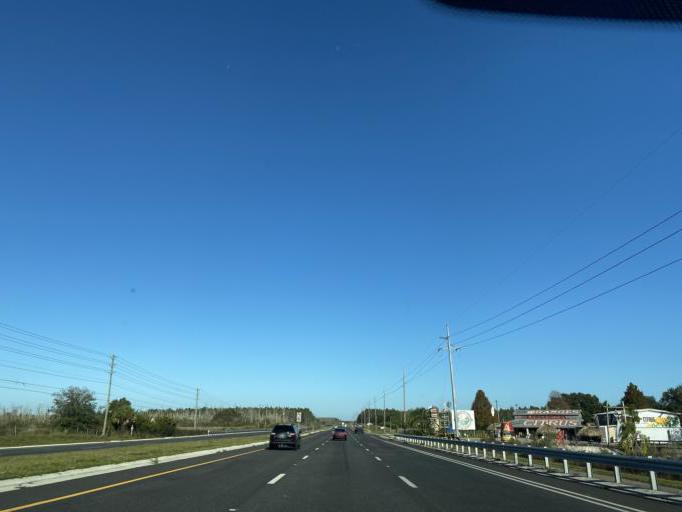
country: US
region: Florida
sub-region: Lake County
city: Four Corners
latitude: 28.4185
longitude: -81.7053
